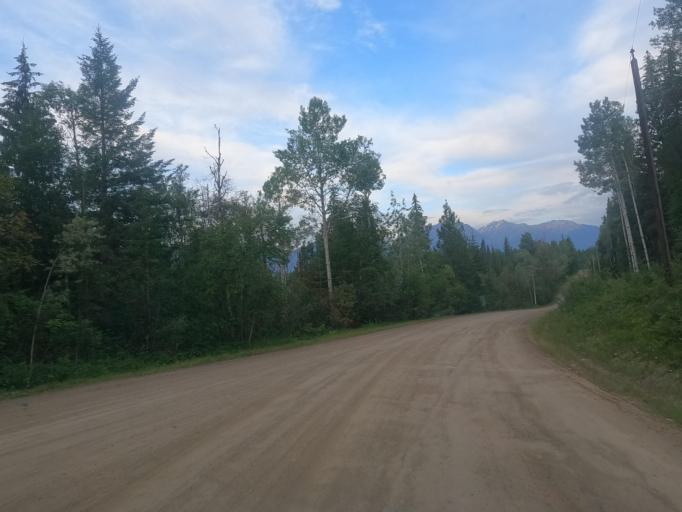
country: CA
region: British Columbia
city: Golden
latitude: 51.4458
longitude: -117.0100
